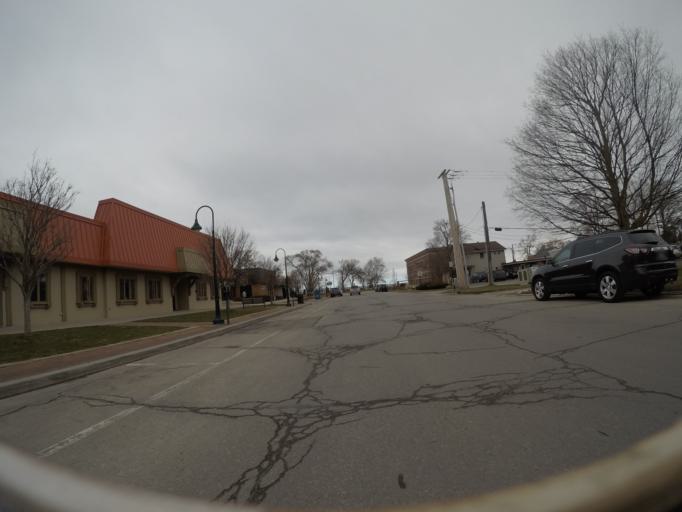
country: US
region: Michigan
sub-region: Grand Traverse County
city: Traverse City
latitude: 44.7632
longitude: -85.6159
